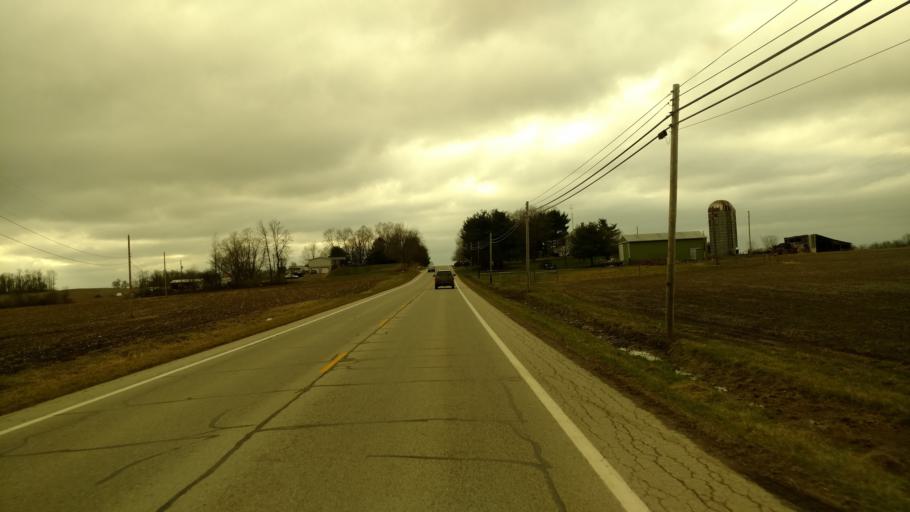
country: US
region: Ohio
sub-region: Licking County
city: Harbor Hills
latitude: 39.9589
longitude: -82.3999
